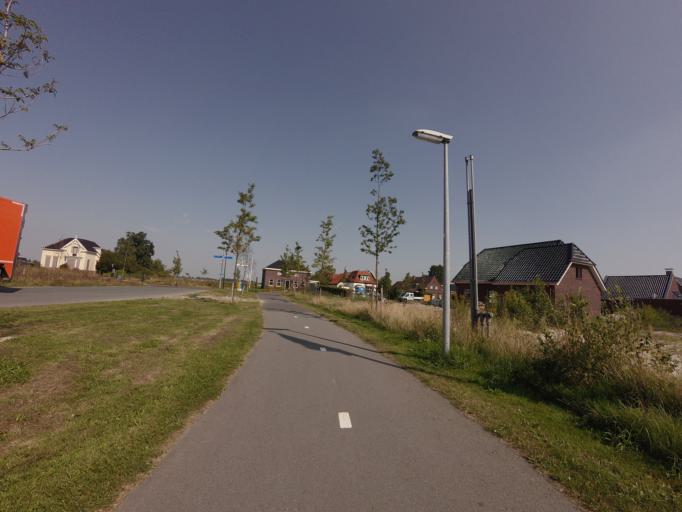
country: NL
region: Groningen
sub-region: Gemeente Zuidhorn
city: Noordhorn
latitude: 53.2575
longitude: 6.3968
